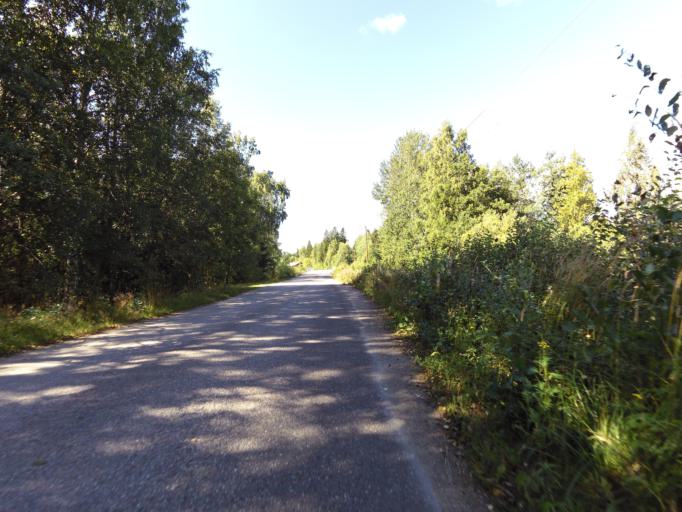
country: SE
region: Gaevleborg
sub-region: Gavle Kommun
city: Valbo
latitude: 60.7693
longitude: 16.9305
